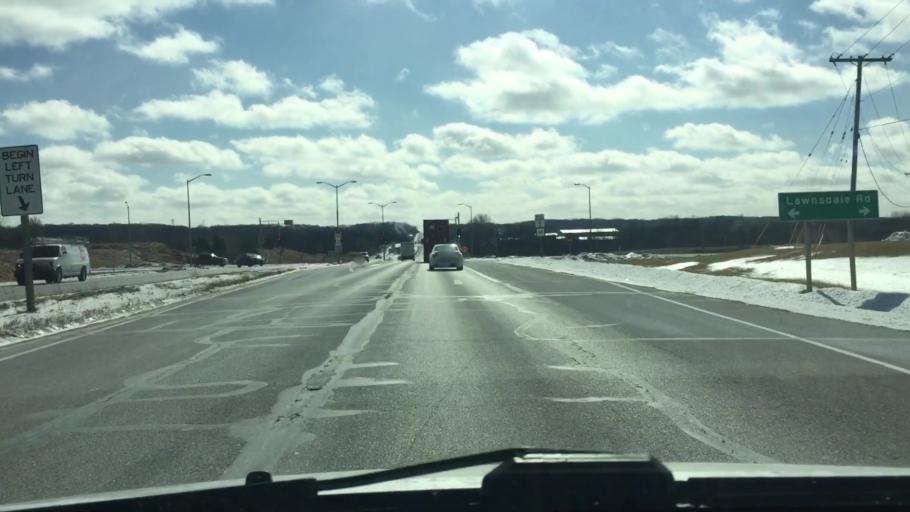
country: US
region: Wisconsin
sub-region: Waukesha County
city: Waukesha
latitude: 42.9605
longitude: -88.2281
